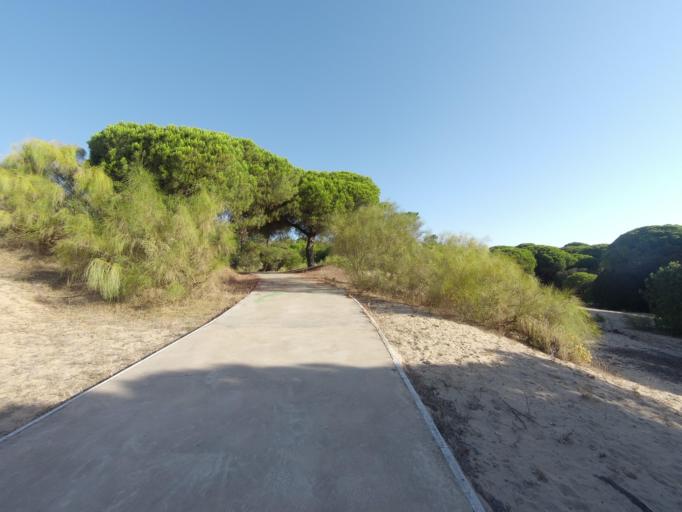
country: ES
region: Andalusia
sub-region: Provincia de Huelva
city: Aljaraque
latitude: 37.2094
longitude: -7.0391
